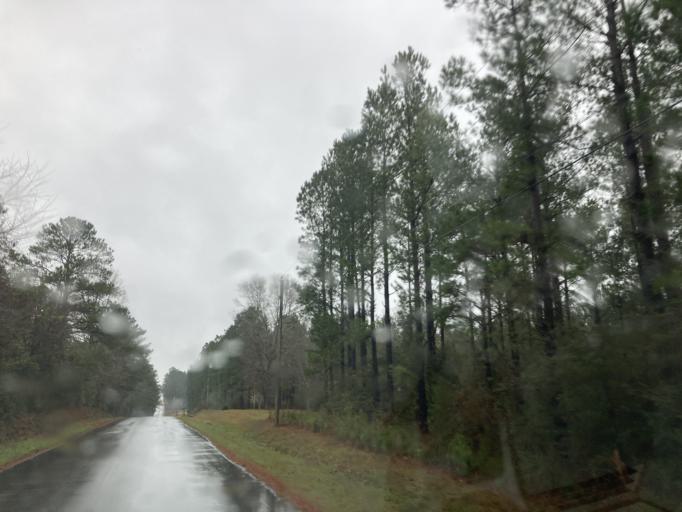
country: US
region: Mississippi
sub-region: Forrest County
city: Rawls Springs
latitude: 31.4669
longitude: -89.3822
